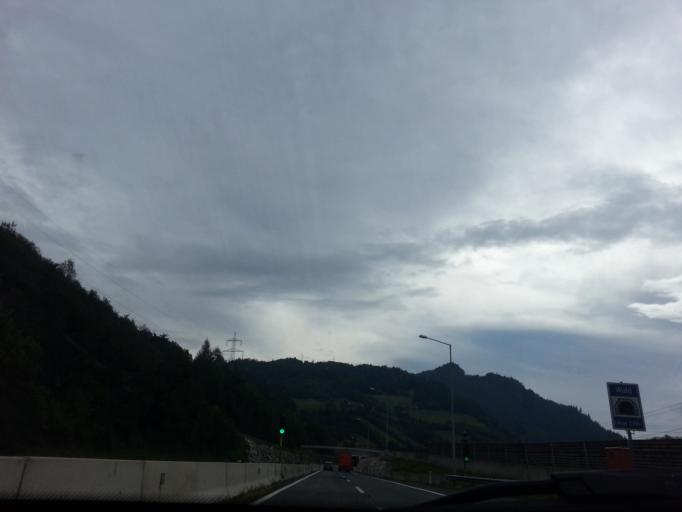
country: AT
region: Styria
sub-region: Politischer Bezirk Leoben
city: Wald am Schoberpass
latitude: 47.4538
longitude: 14.6643
